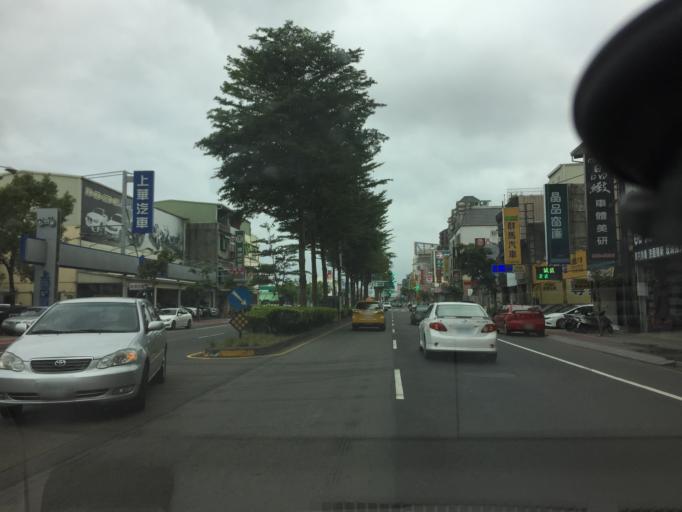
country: TW
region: Taiwan
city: Taoyuan City
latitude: 24.9930
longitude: 121.2751
